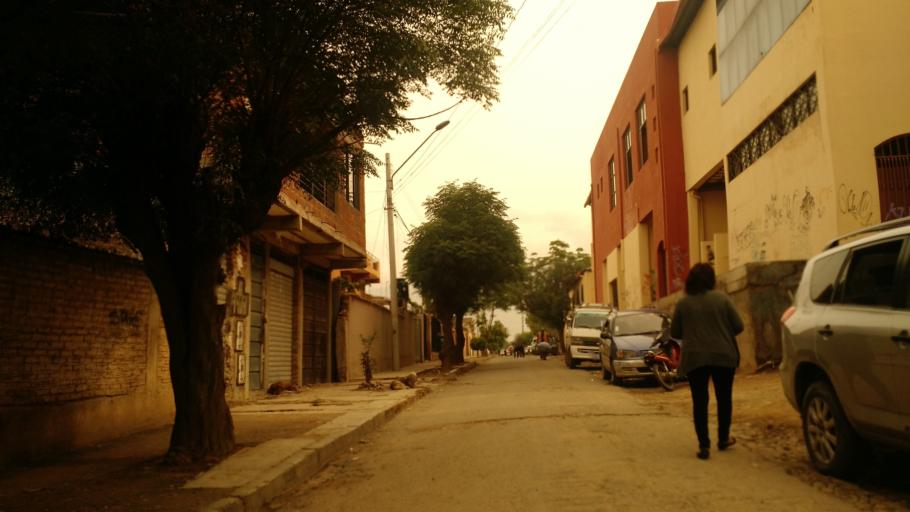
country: BO
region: Cochabamba
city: Cochabamba
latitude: -17.4282
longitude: -66.1564
